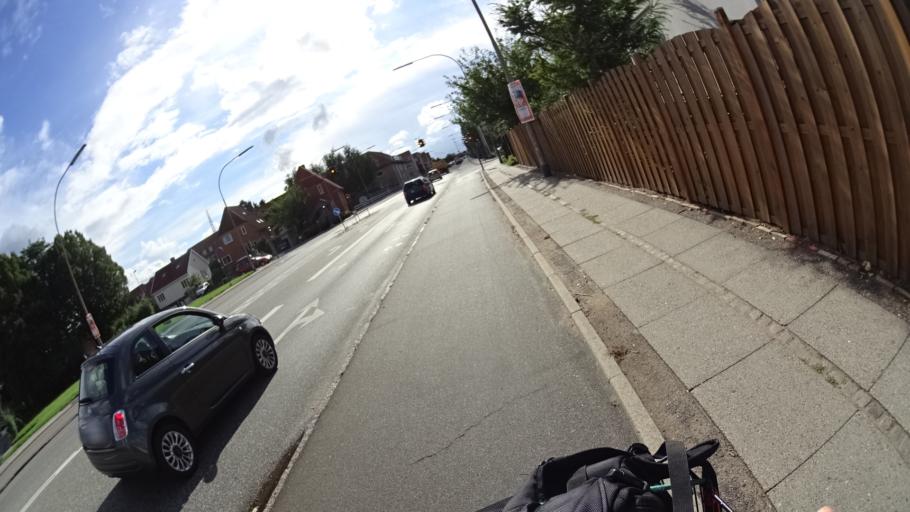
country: DK
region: Central Jutland
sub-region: Arhus Kommune
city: Stavtrup
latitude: 56.1489
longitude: 10.1611
